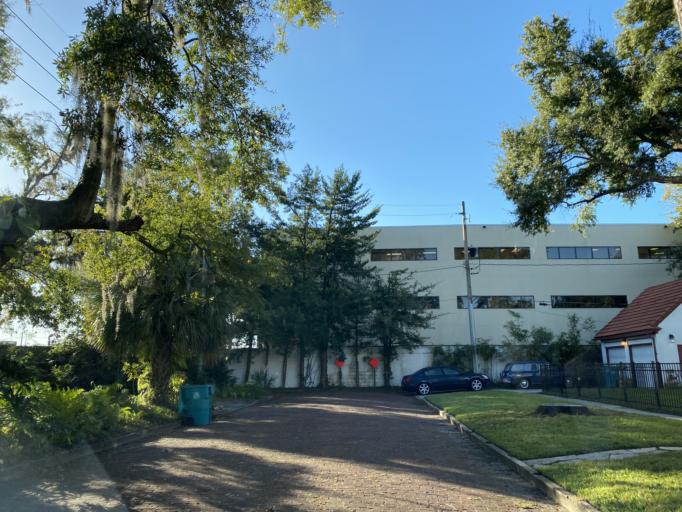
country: US
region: Florida
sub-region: Orange County
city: Orlando
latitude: 28.5538
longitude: -81.3961
